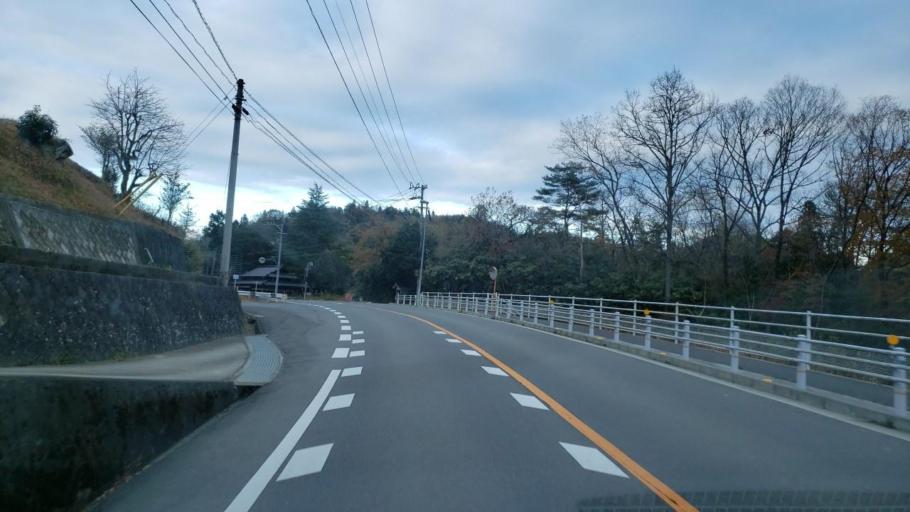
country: JP
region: Tokushima
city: Wakimachi
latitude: 34.1732
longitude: 134.1666
